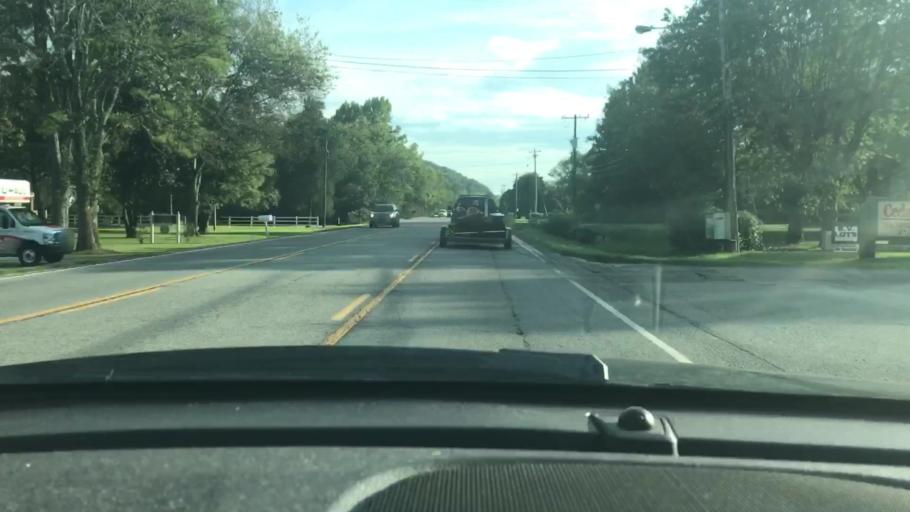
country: US
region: Tennessee
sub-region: Sumner County
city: Millersville
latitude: 36.3615
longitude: -86.7123
